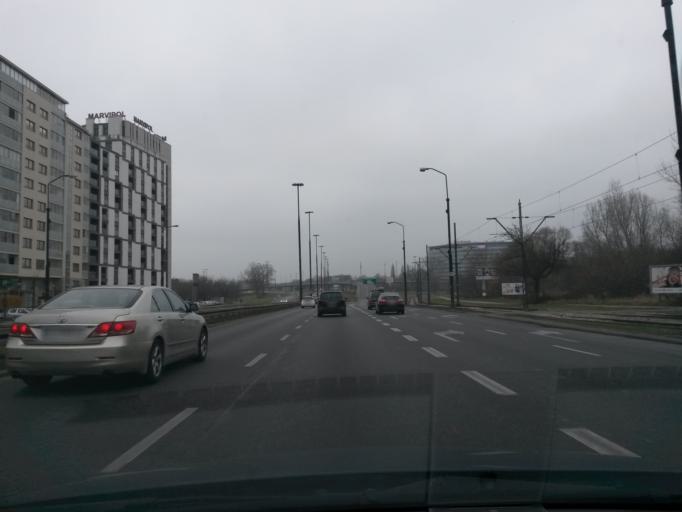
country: PL
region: Masovian Voivodeship
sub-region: Warszawa
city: Mokotow
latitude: 52.1708
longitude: 21.0190
